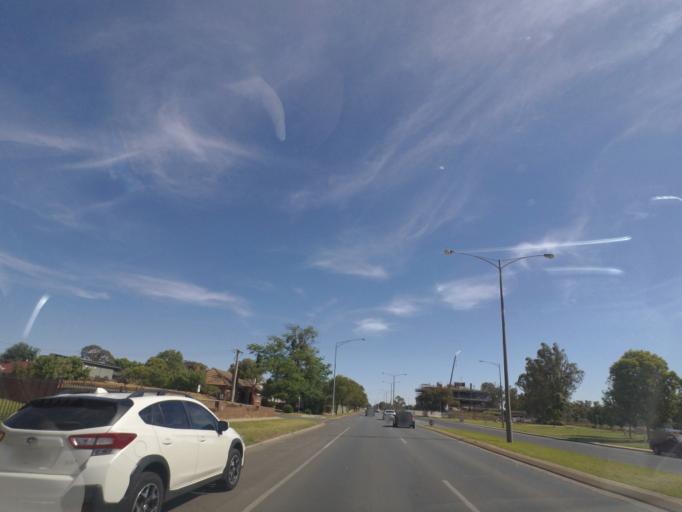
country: AU
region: Victoria
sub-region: Greater Shepparton
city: Shepparton
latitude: -36.3889
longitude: 145.3978
